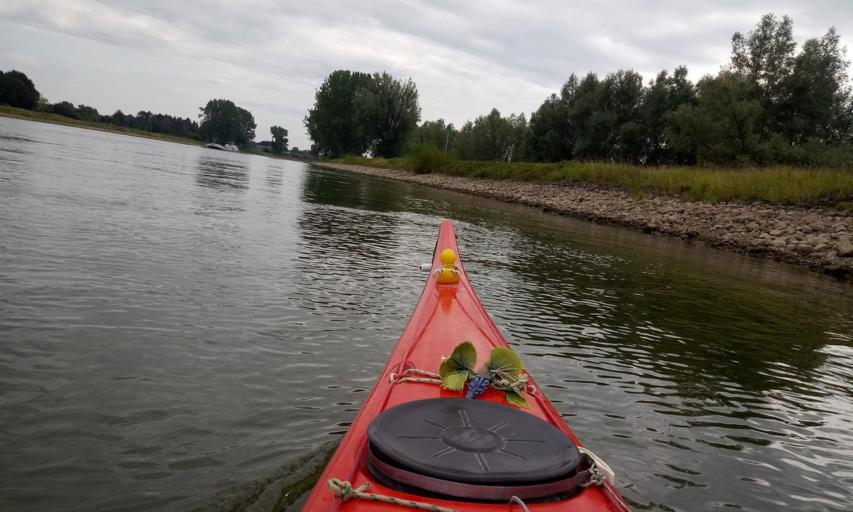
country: NL
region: Gelderland
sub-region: Gemeente Lochem
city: Epse
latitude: 52.2203
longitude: 6.1834
